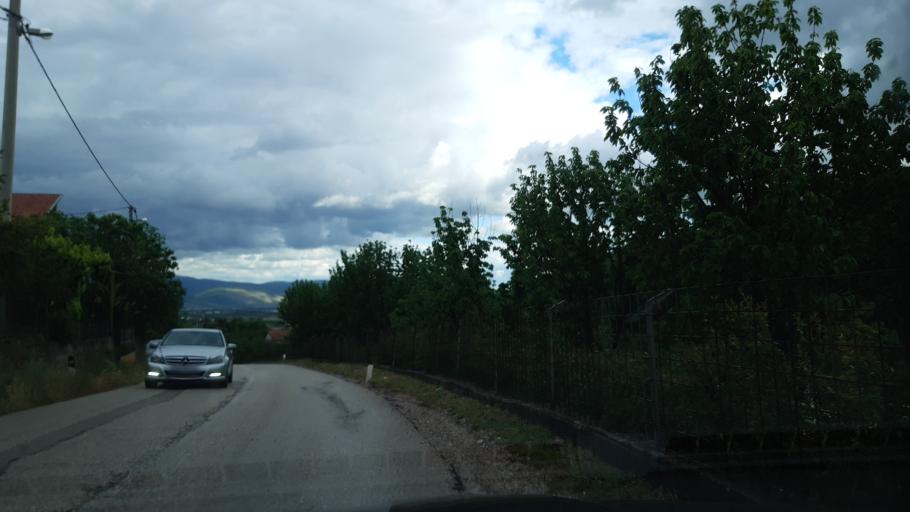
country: BA
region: Federation of Bosnia and Herzegovina
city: Rodoc
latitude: 43.3077
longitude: 17.7909
